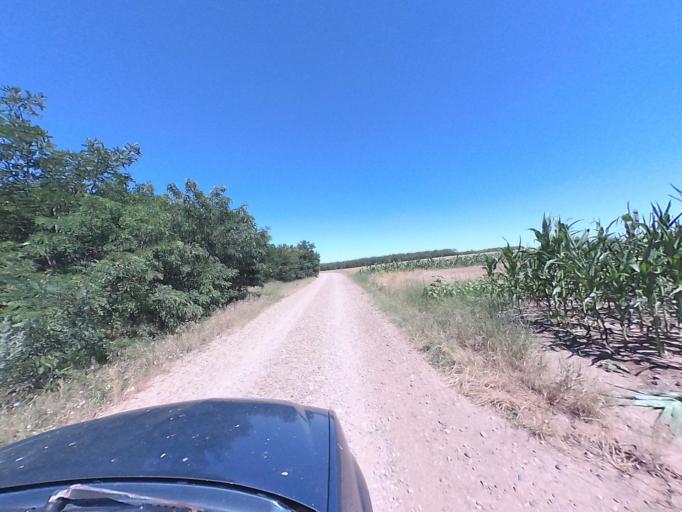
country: RO
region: Vaslui
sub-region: Comuna Costesti
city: Costesti
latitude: 46.4829
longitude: 27.7736
